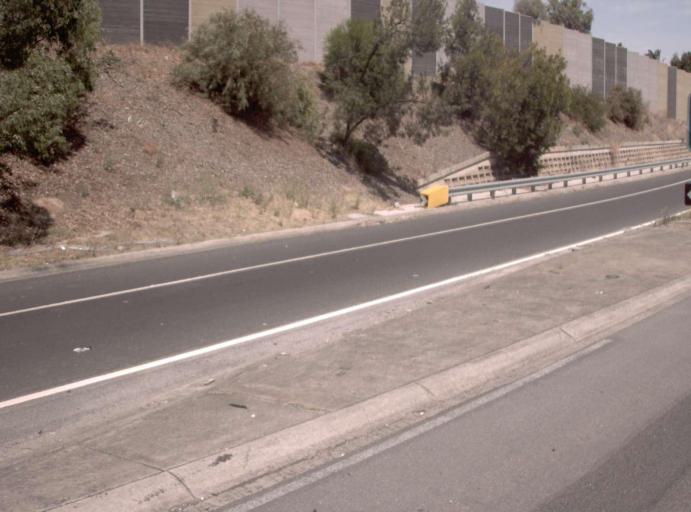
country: AU
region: Victoria
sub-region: Monash
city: Chadstone
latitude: -37.8874
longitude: 145.1108
